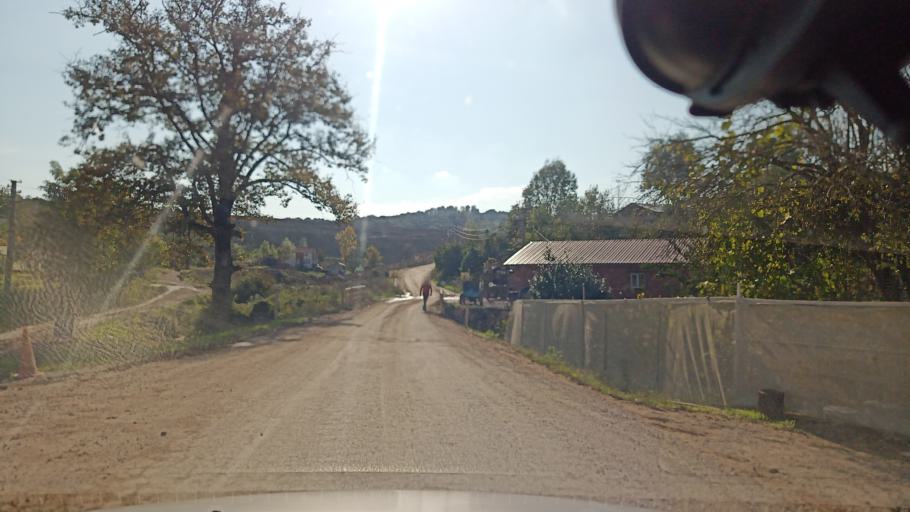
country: TR
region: Sakarya
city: Ferizli
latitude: 41.1054
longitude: 30.4759
